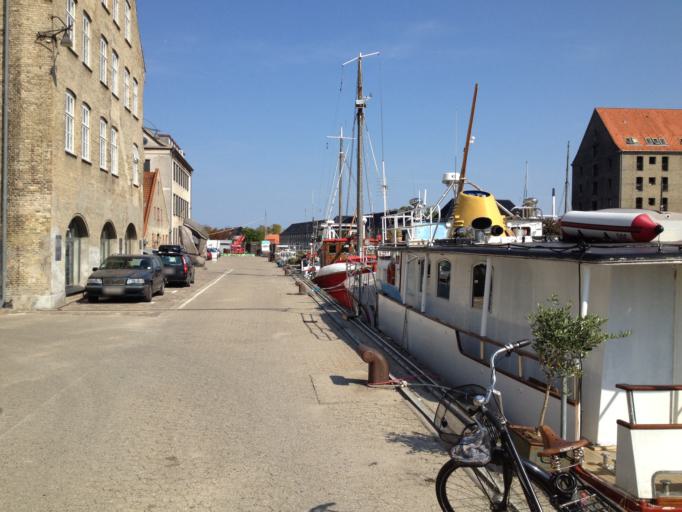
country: DK
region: Capital Region
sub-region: Kobenhavn
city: Christianshavn
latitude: 55.6768
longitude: 12.5972
